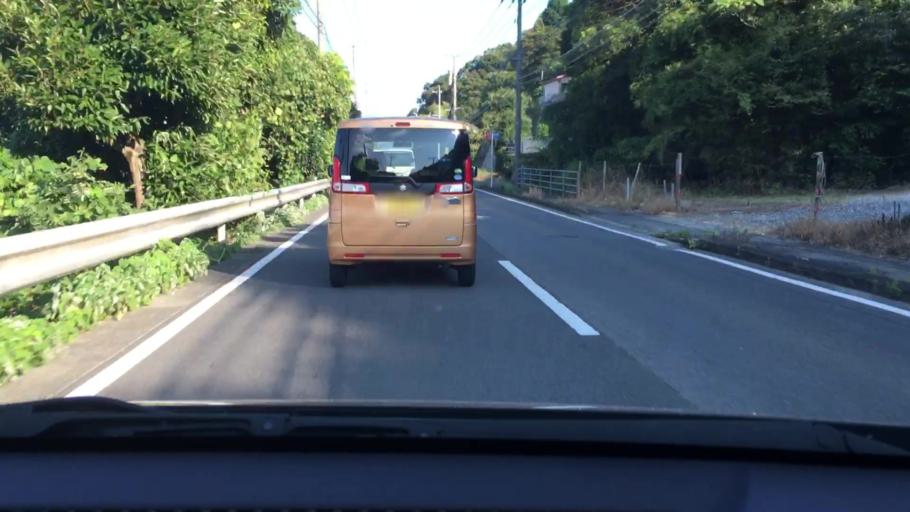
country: JP
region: Nagasaki
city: Togitsu
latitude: 32.8907
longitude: 129.7830
